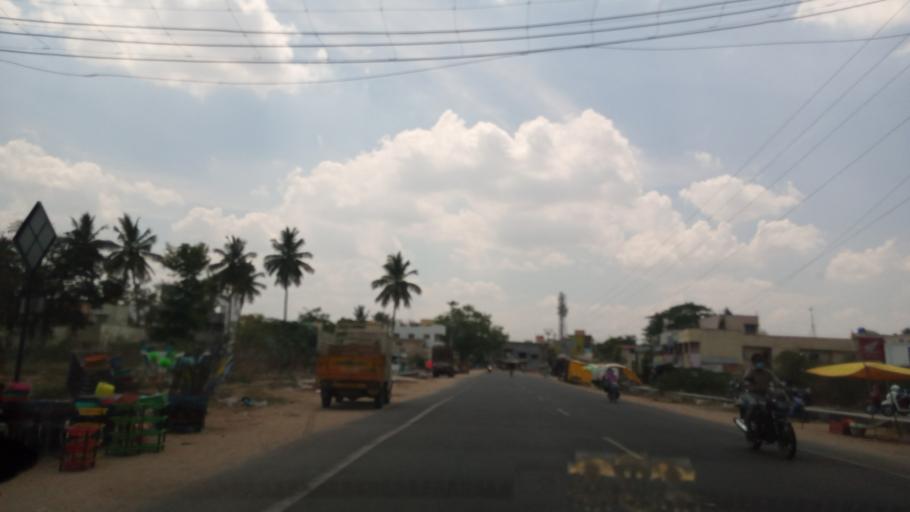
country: IN
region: Tamil Nadu
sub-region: Vellore
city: Walajapet
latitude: 12.9237
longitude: 79.3729
